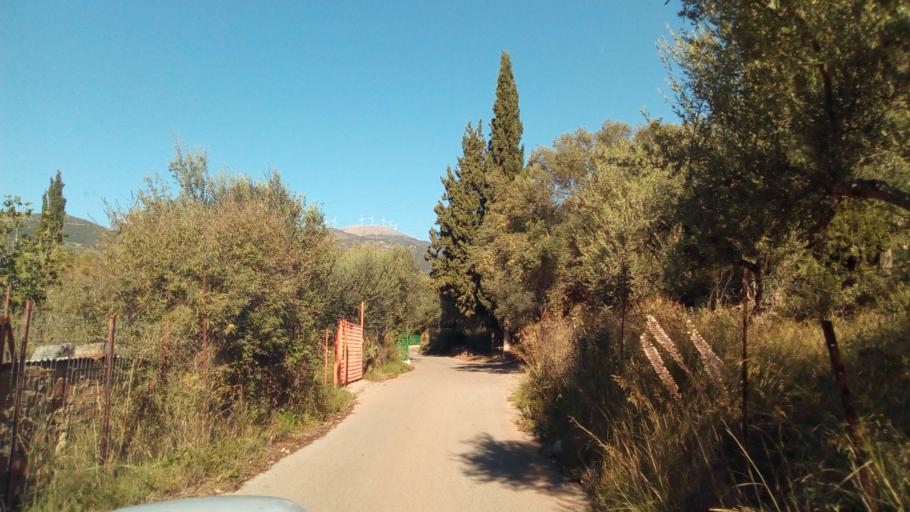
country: GR
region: West Greece
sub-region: Nomos Aitolias kai Akarnanias
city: Nafpaktos
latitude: 38.4041
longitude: 21.8571
